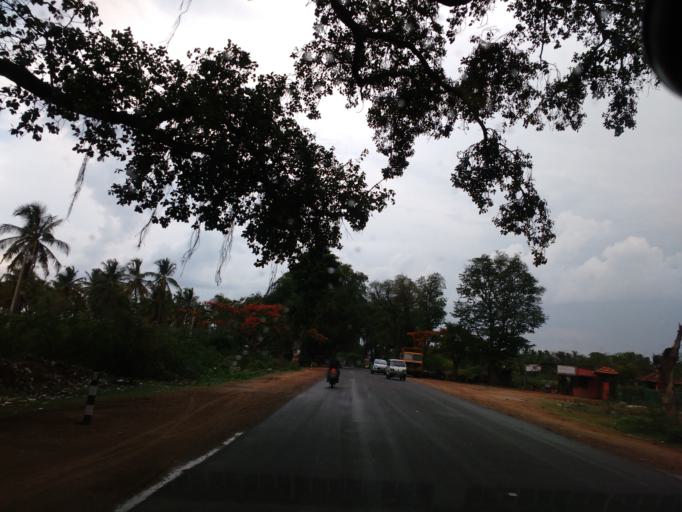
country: IN
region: Karnataka
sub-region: Chikmagalur
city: Kadur
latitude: 13.5400
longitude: 76.0231
